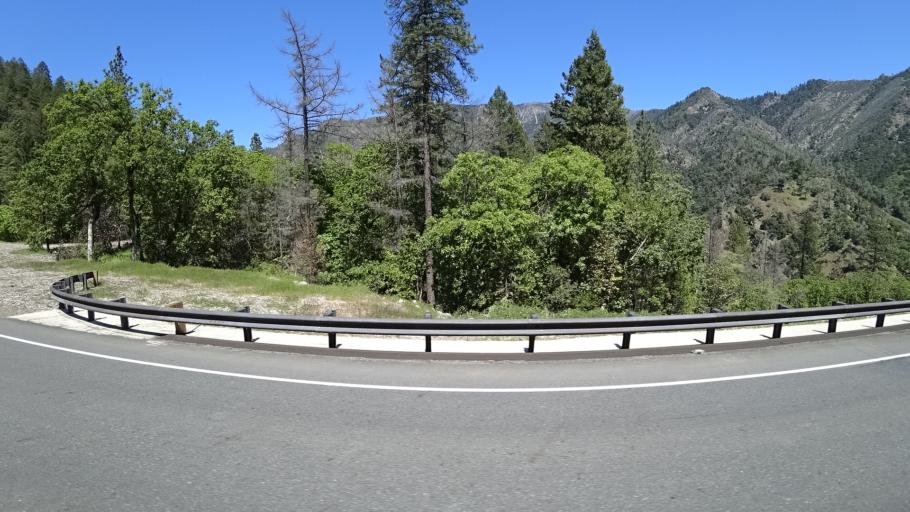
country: US
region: California
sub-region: Humboldt County
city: Willow Creek
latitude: 40.8006
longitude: -123.4648
